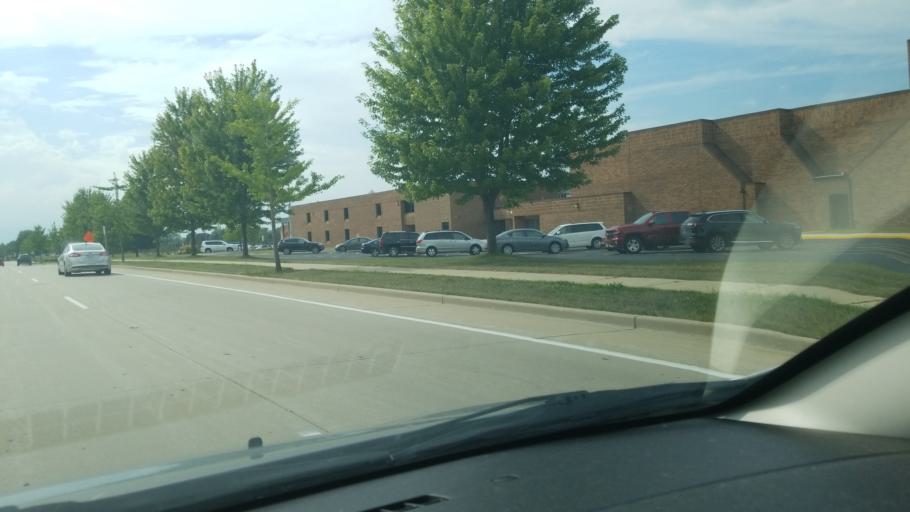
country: US
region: Wisconsin
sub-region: Ozaukee County
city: Grafton
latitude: 43.3202
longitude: -87.9389
